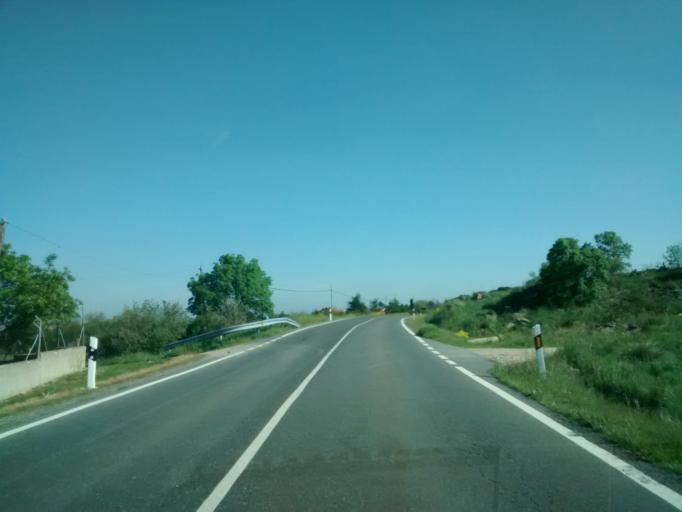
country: ES
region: Castille and Leon
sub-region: Provincia de Segovia
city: Palazuelos de Eresma
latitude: 40.9325
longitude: -4.0329
